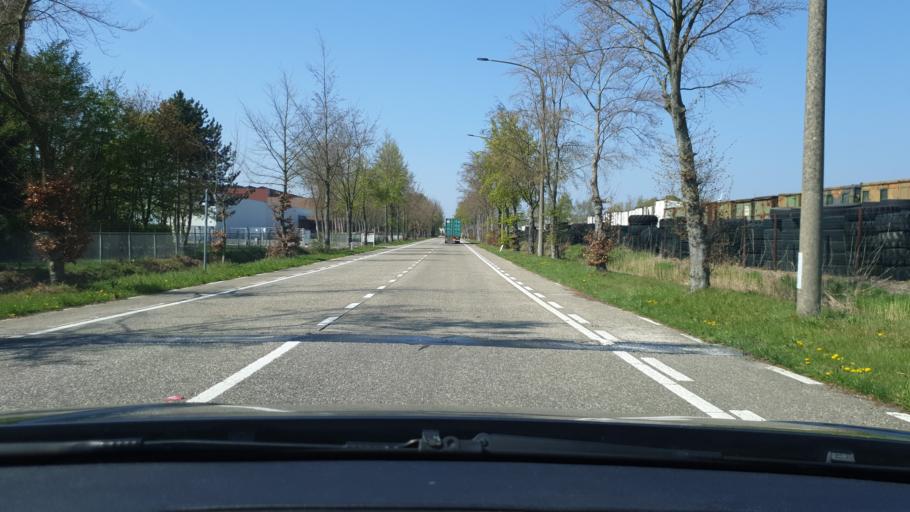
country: BE
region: Flanders
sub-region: Provincie Antwerpen
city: Westerlo
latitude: 51.1242
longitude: 4.9488
